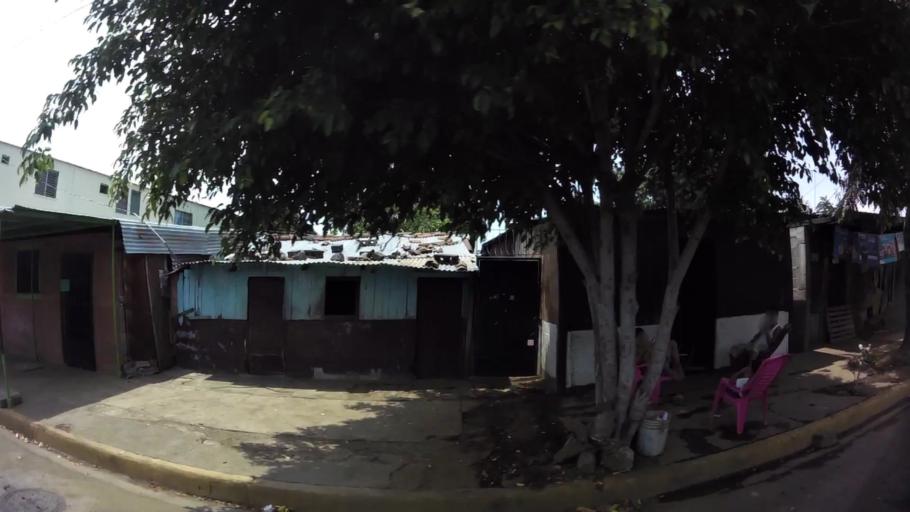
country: NI
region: Managua
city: Managua
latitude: 12.1489
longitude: -86.2916
